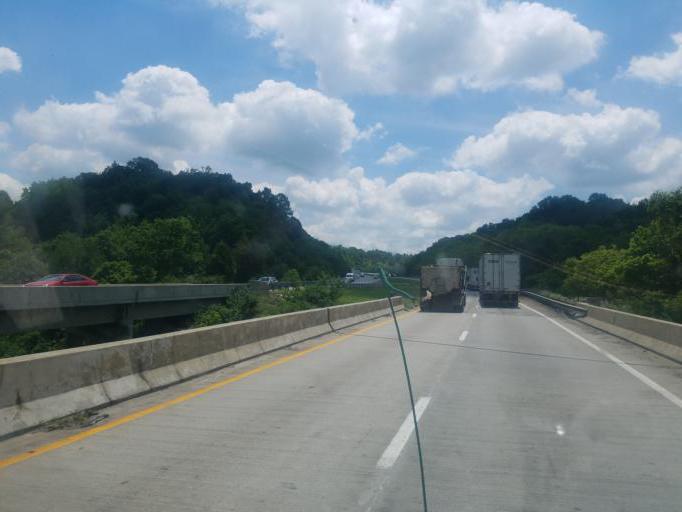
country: US
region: Kentucky
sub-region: Trimble County
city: Providence
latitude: 38.5925
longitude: -85.1756
